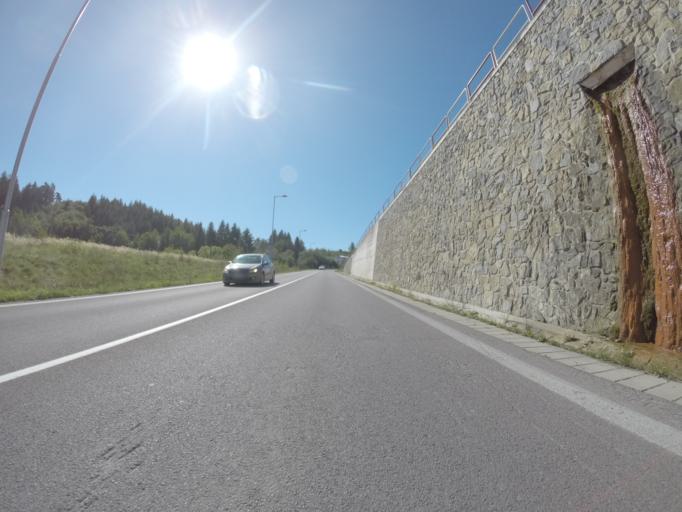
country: SK
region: Trenciansky
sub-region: Okres Povazska Bystrica
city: Povazska Bystrica
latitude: 49.1020
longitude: 18.4528
